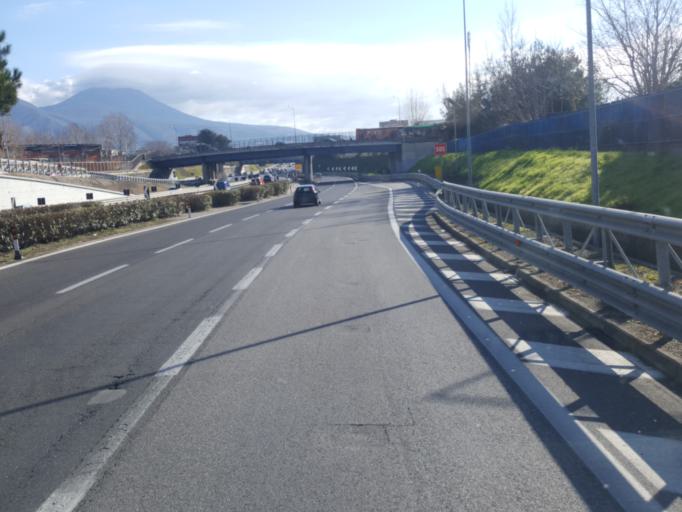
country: IT
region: Campania
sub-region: Provincia di Napoli
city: San Giorgio a Cremano
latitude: 40.8476
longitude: 14.3164
